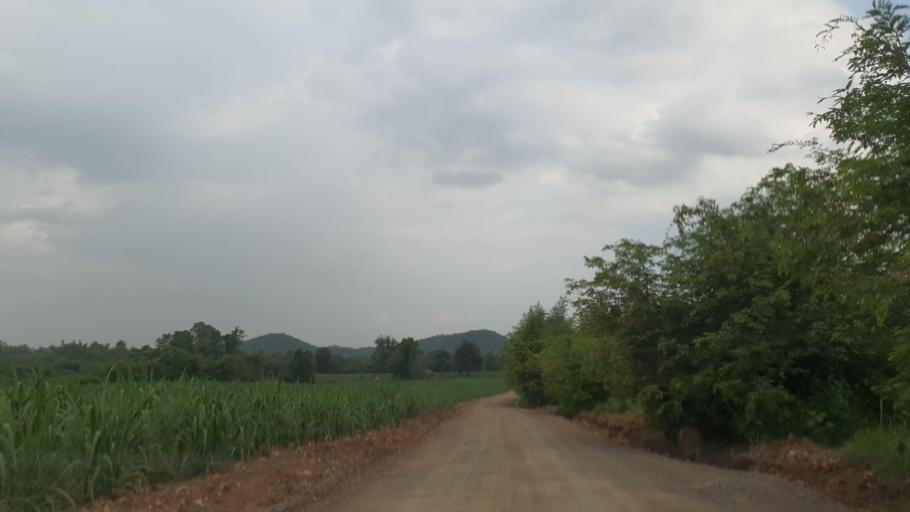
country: TH
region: Sukhothai
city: Thung Saliam
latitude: 17.2561
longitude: 99.5412
